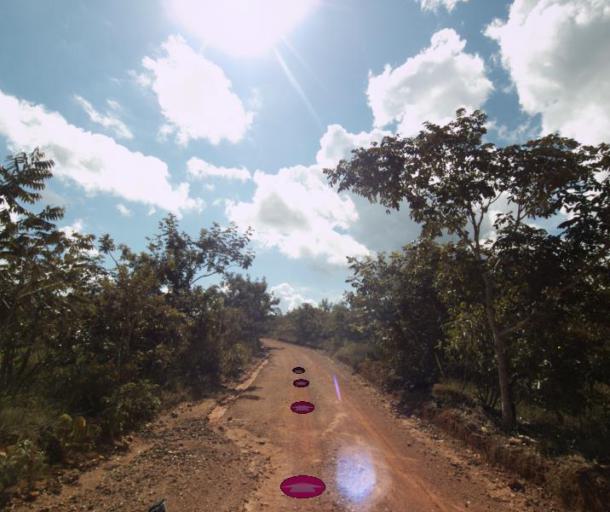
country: BR
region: Goias
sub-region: Pirenopolis
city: Pirenopolis
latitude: -15.7757
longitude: -48.9941
